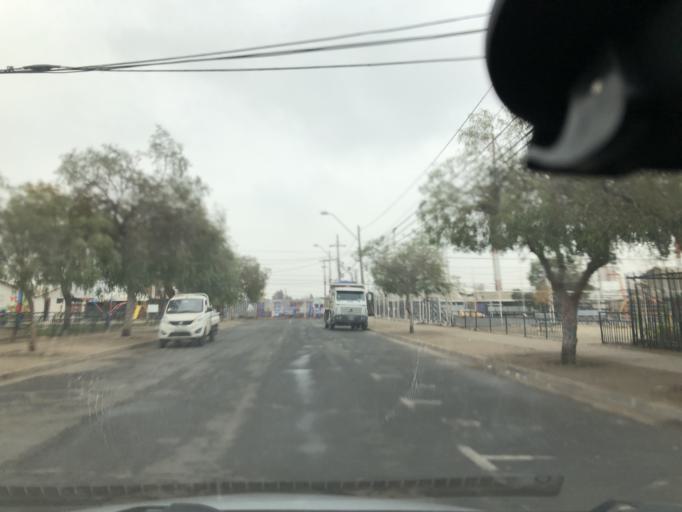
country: CL
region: Santiago Metropolitan
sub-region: Provincia de Cordillera
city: Puente Alto
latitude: -33.5830
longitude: -70.5933
